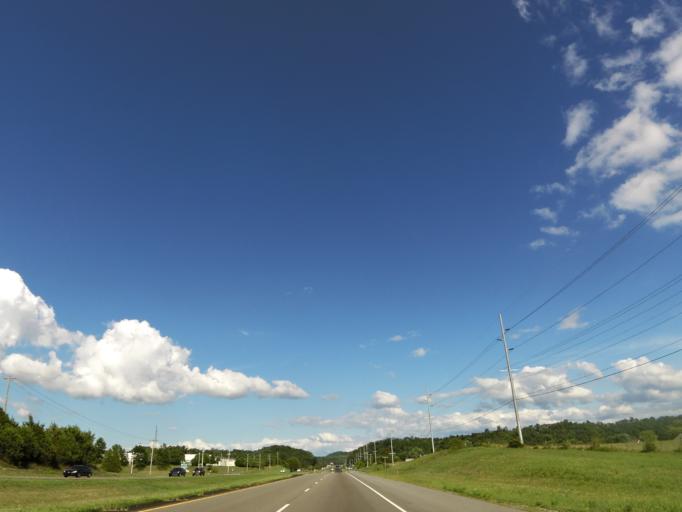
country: US
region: Tennessee
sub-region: Greene County
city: Mosheim
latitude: 36.1728
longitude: -82.9048
